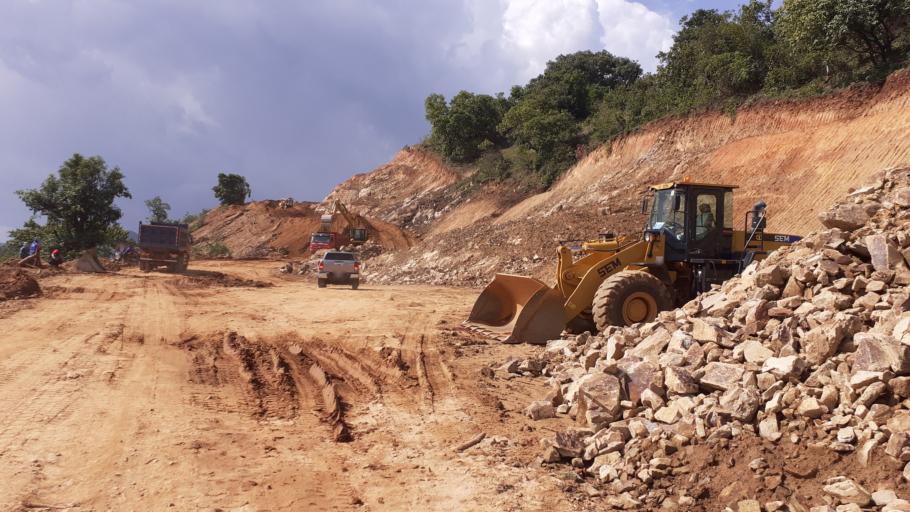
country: ET
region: Oromiya
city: Gimbi
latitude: 9.3257
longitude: 35.6921
